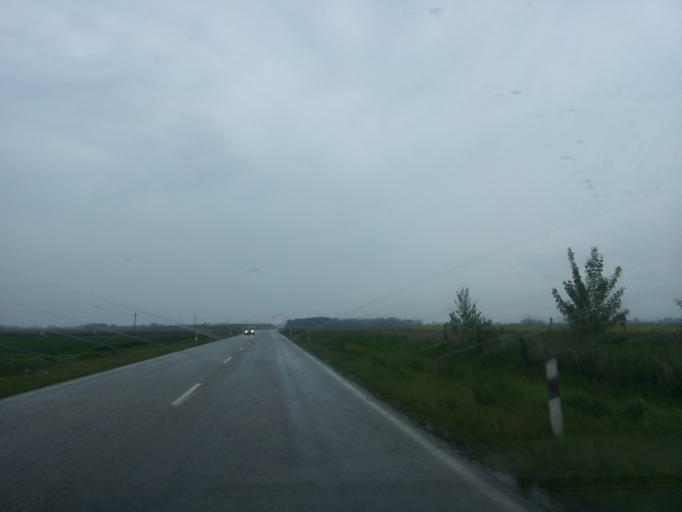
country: HU
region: Tolna
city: Szekszard
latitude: 46.3082
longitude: 18.7075
